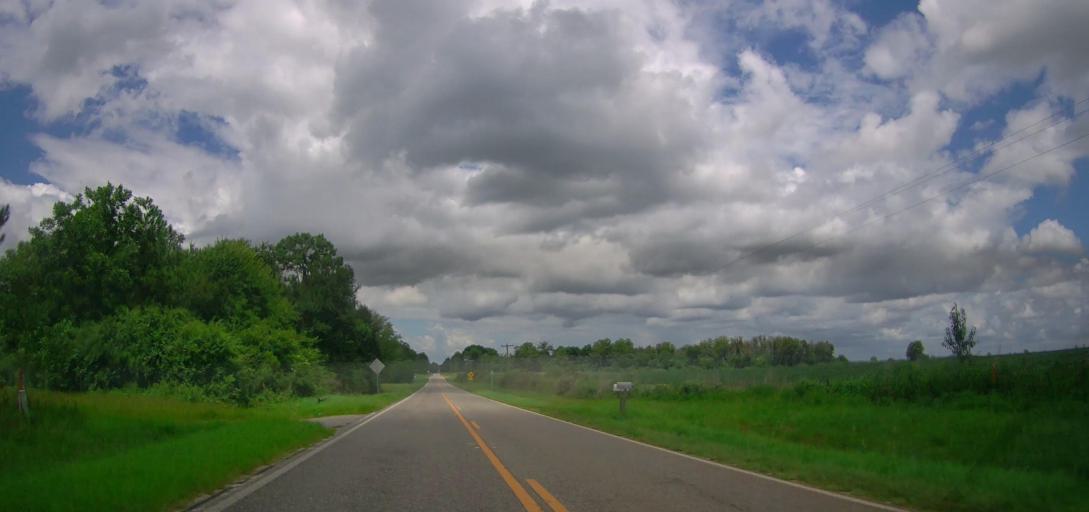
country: US
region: Georgia
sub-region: Wilcox County
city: Rochelle
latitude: 31.8964
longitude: -83.5530
